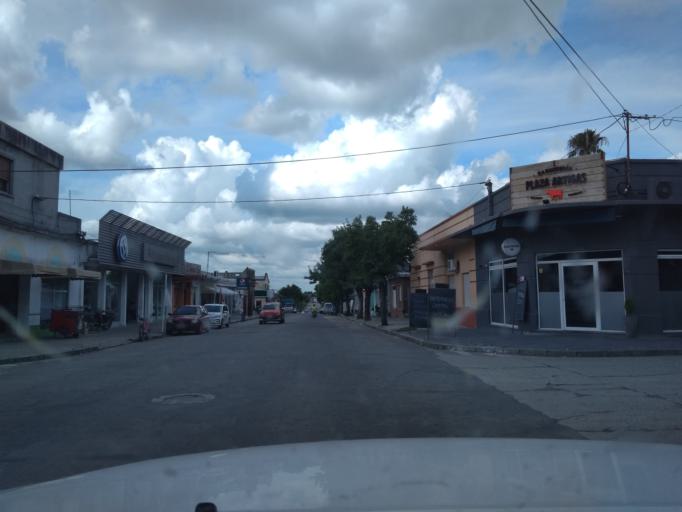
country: UY
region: Florida
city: Florida
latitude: -34.0932
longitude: -56.2187
